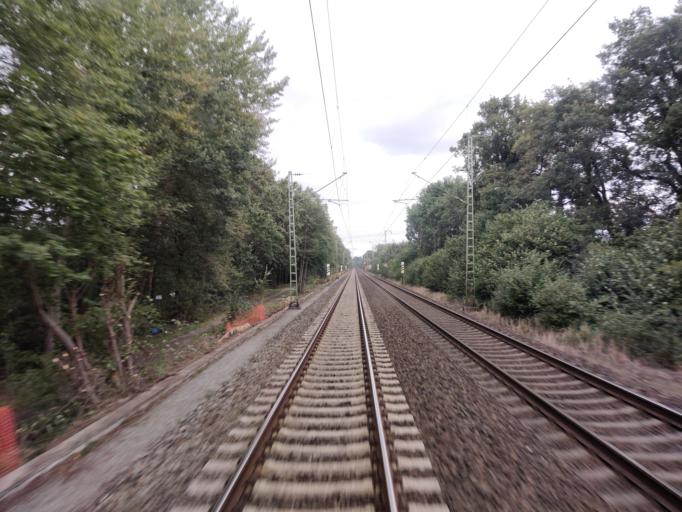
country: DE
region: Lower Saxony
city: Osterholz-Scharmbeck
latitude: 53.2047
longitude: 8.7754
